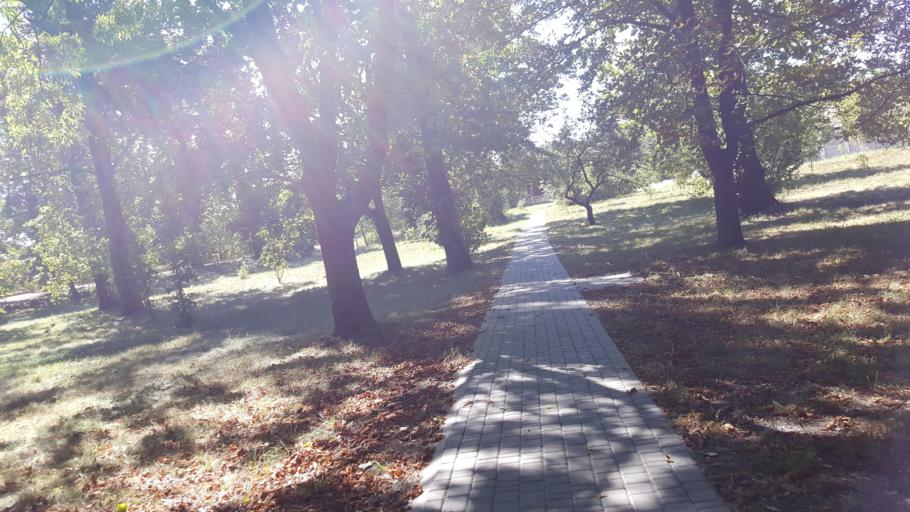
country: BY
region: Brest
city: Vysokaye
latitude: 52.2211
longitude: 23.4520
